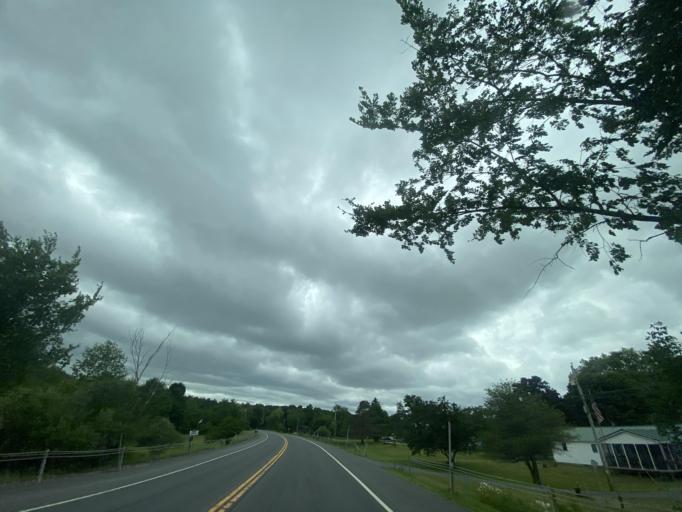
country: US
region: New York
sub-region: Greene County
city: Cairo
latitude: 42.3974
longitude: -73.9814
